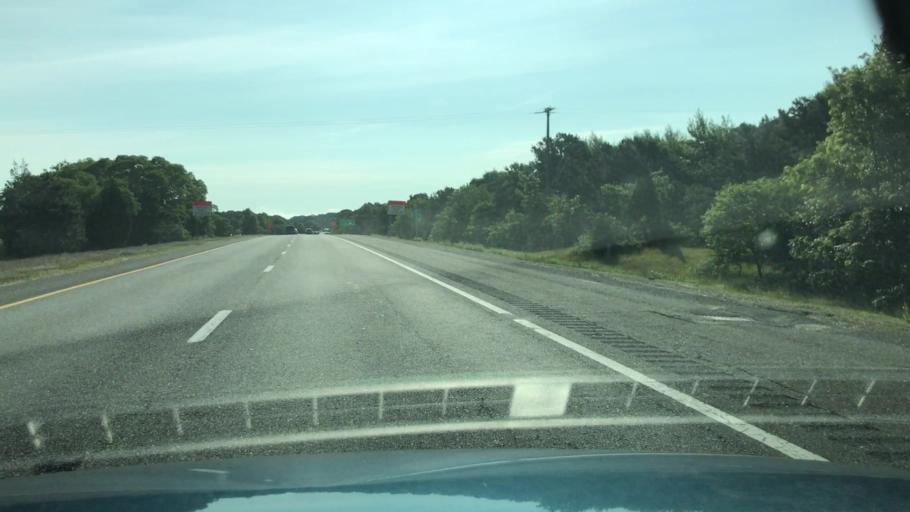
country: US
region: Massachusetts
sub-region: Barnstable County
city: South Dennis
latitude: 41.6925
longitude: -70.1766
